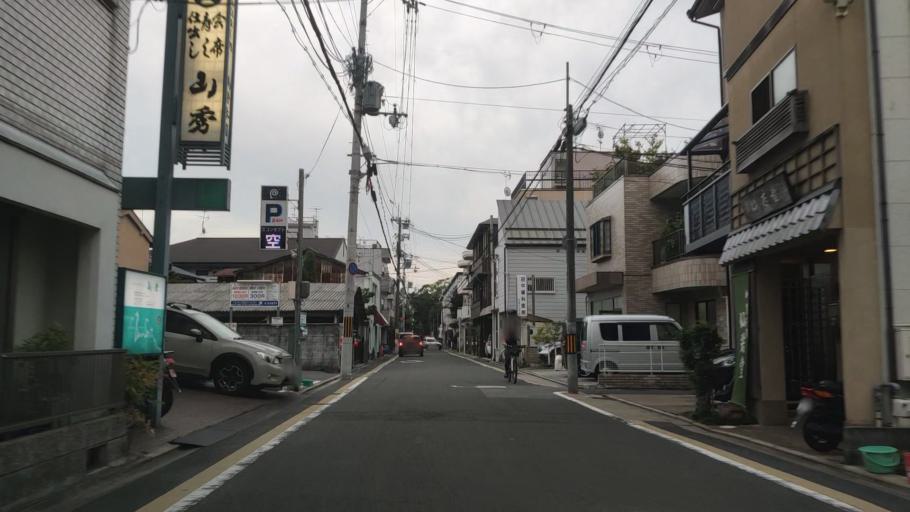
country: JP
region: Kyoto
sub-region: Kyoto-shi
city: Kamigyo-ku
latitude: 35.0194
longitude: 135.7825
